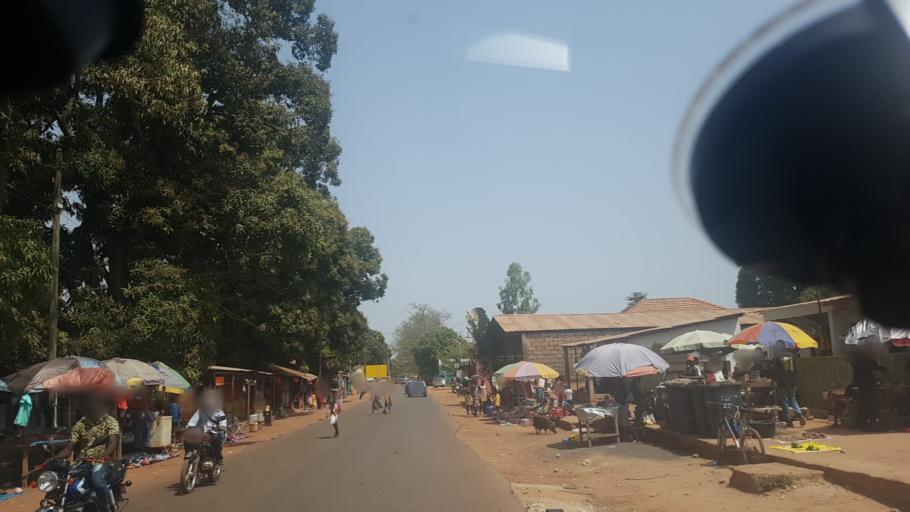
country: GW
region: Bissau
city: Bissau
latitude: 11.9540
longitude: -15.6489
